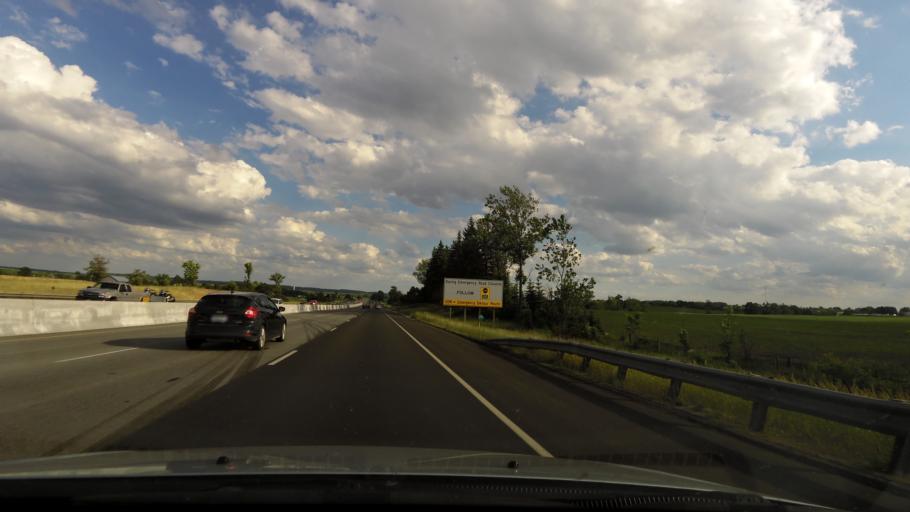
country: CA
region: Ontario
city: Innisfil
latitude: 44.2177
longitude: -79.6619
